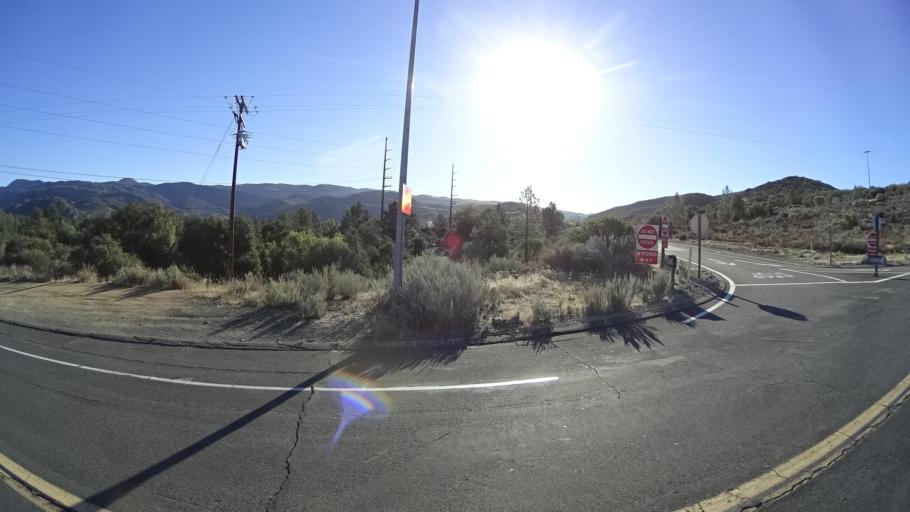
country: US
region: California
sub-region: San Diego County
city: Pine Valley
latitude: 32.8195
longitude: -116.5325
